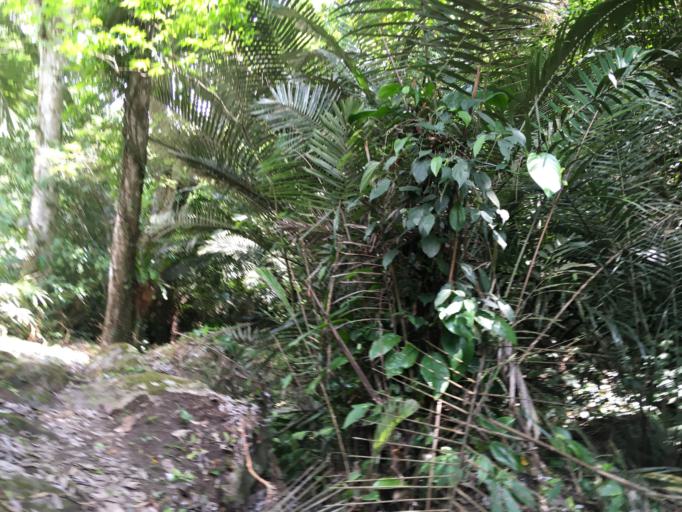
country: TW
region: Taiwan
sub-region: Yilan
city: Yilan
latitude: 24.4287
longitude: 121.6937
